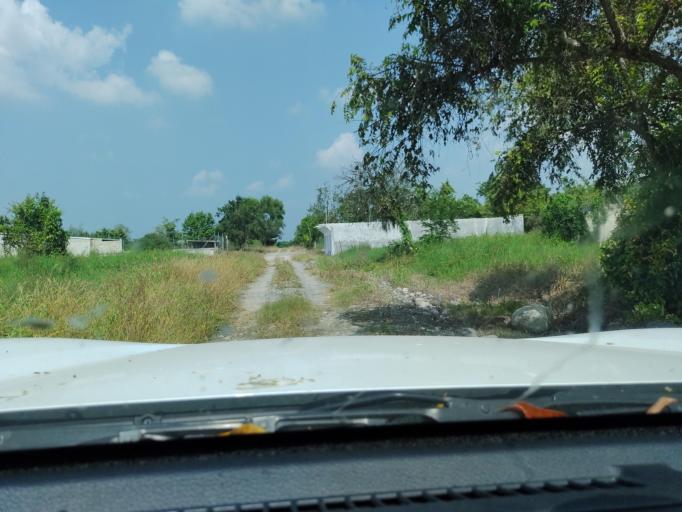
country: MX
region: Veracruz
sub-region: Martinez de la Torre
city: El Progreso
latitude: 20.0691
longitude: -97.0083
